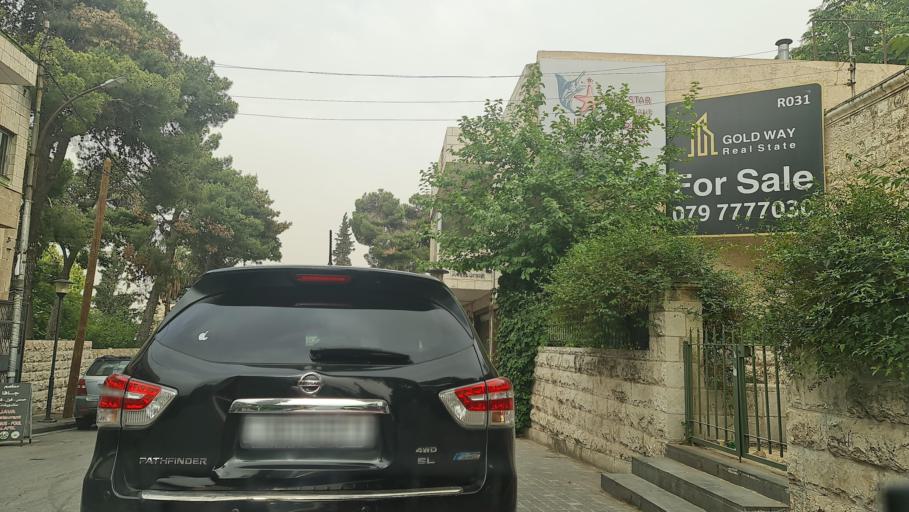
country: JO
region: Amman
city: Amman
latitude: 31.9490
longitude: 35.9283
